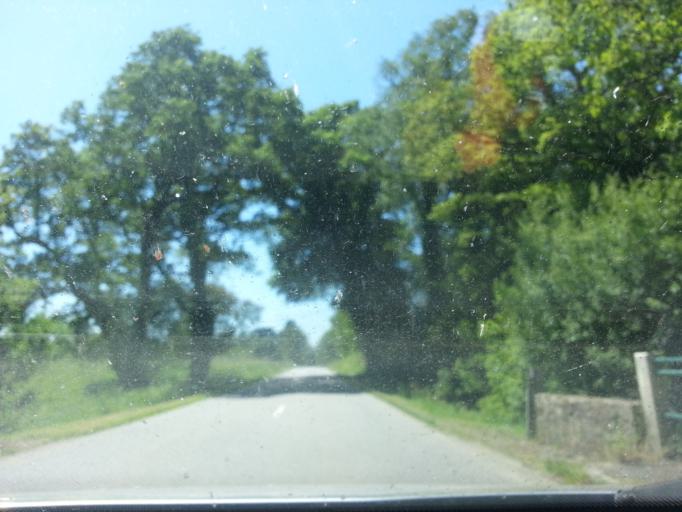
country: FR
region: Brittany
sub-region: Departement du Morbihan
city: Langonnet
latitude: 48.0786
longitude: -3.4644
